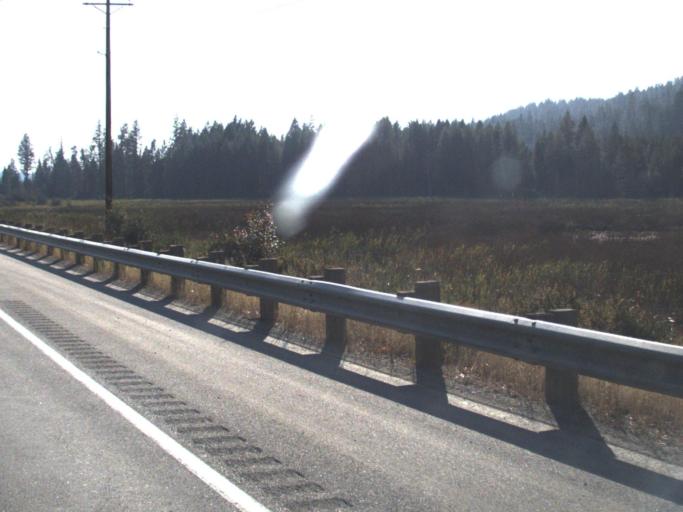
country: US
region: Washington
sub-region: Pend Oreille County
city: Newport
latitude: 48.1664
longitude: -117.0809
